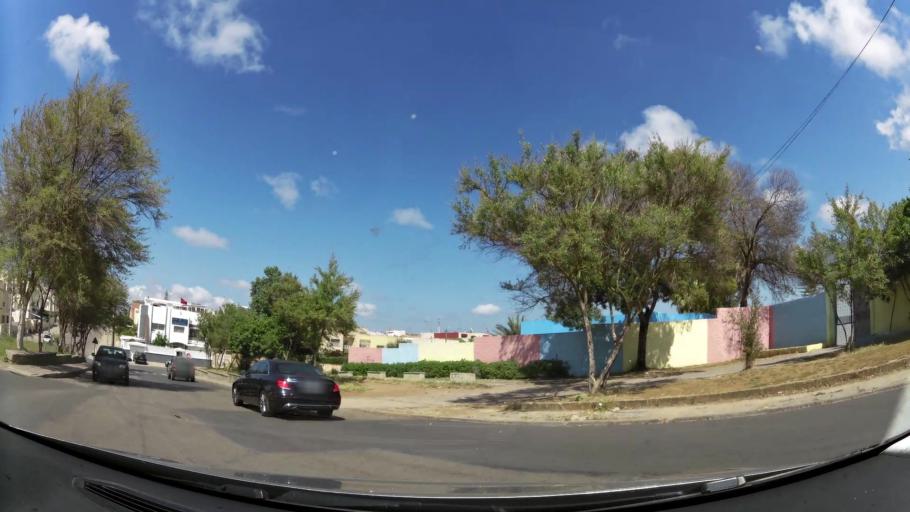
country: MA
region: Rabat-Sale-Zemmour-Zaer
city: Sale
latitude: 34.0372
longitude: -6.7912
